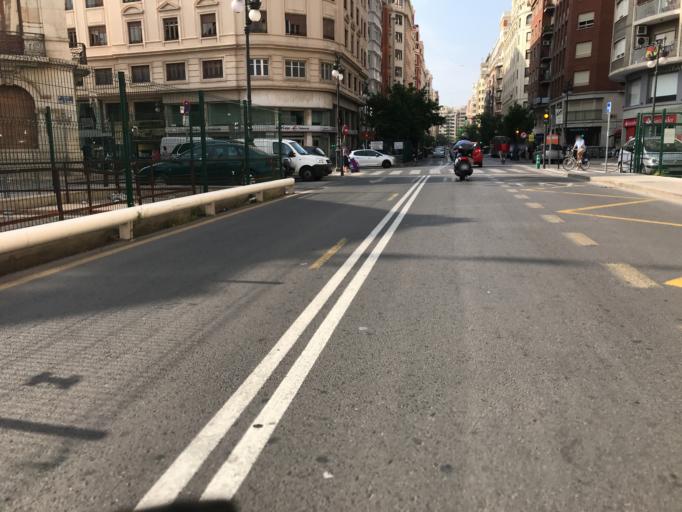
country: ES
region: Valencia
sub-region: Provincia de Valencia
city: Valencia
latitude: 39.4735
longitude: -0.3798
